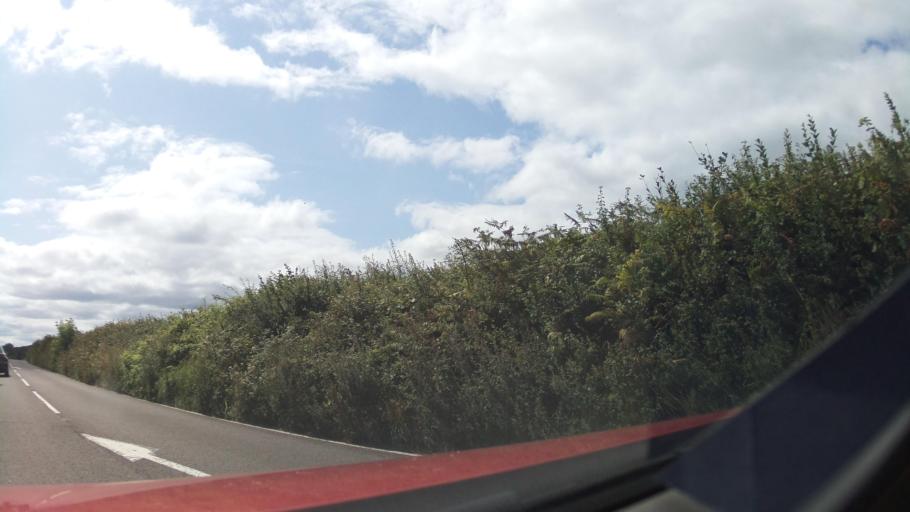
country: GB
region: England
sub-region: Devon
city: Teignmouth
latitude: 50.5241
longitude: -3.5100
